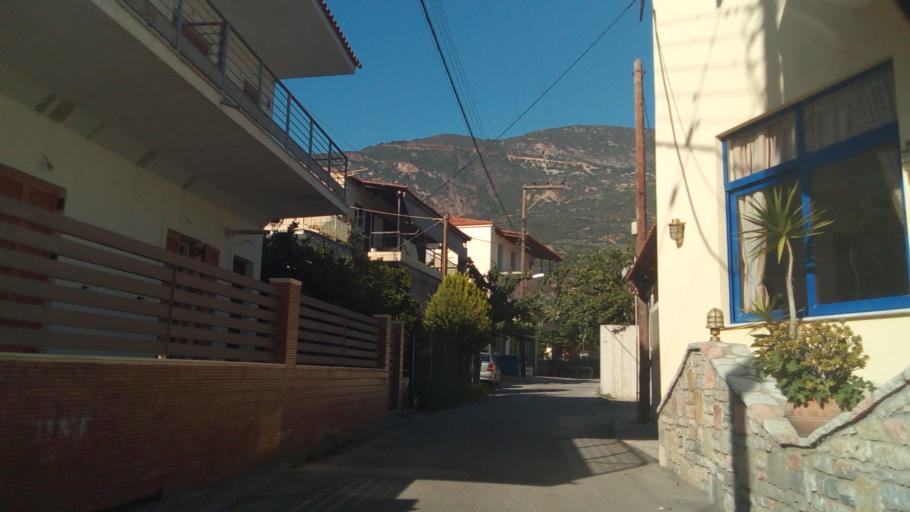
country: GR
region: West Greece
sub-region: Nomos Achaias
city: Selianitika
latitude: 38.3816
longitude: 22.0756
